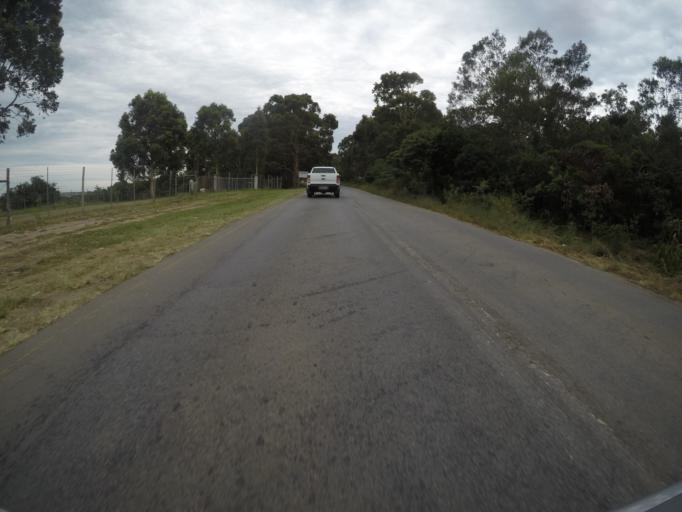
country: ZA
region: Eastern Cape
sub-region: Buffalo City Metropolitan Municipality
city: East London
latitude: -32.9381
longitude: 27.9422
